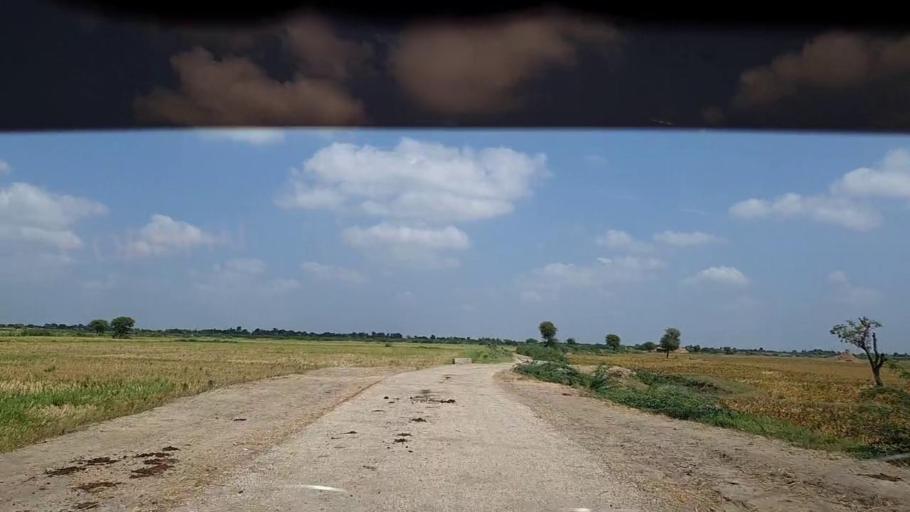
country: PK
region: Sindh
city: Kadhan
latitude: 24.5824
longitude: 68.9648
